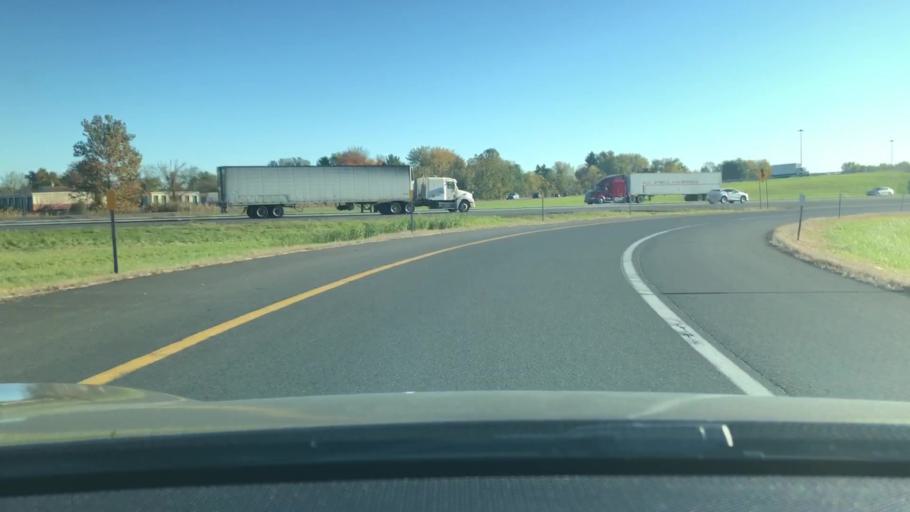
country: US
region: New York
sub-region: Ulster County
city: Lincoln Park
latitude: 41.9497
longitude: -74.0258
